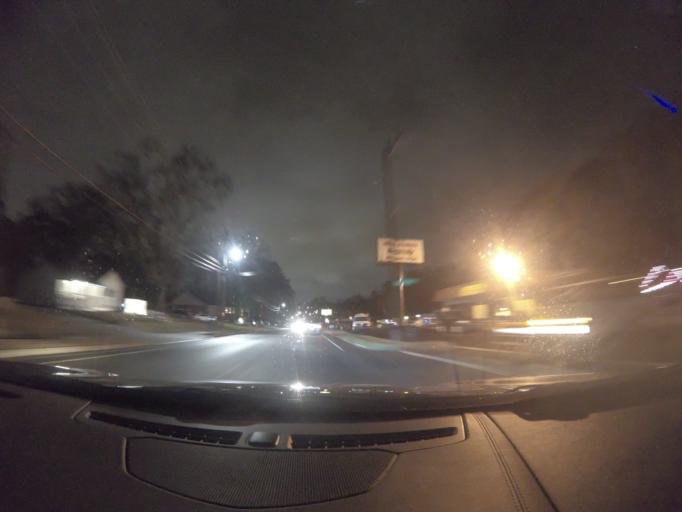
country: US
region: Georgia
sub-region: Cobb County
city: Acworth
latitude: 34.0627
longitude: -84.6665
